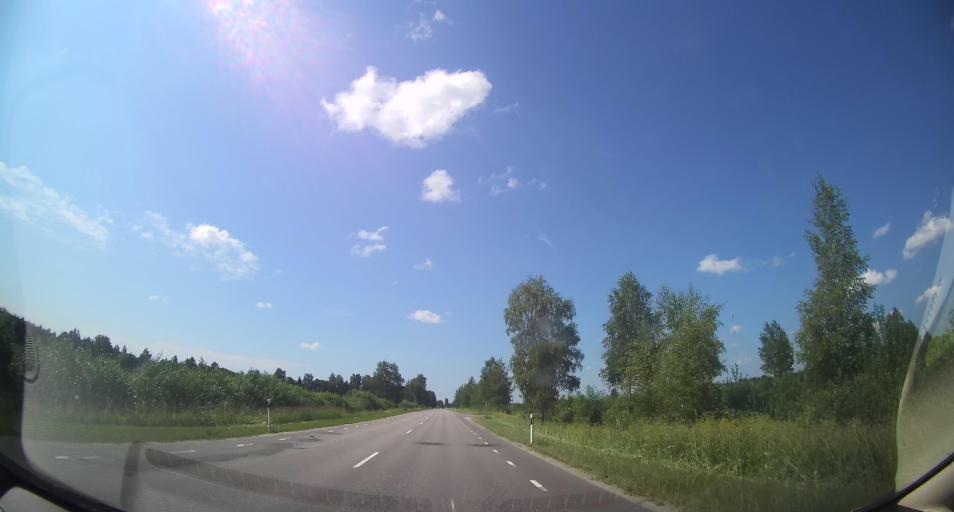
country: EE
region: Raplamaa
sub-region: Rapla vald
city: Rapla
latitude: 58.9586
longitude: 24.7049
